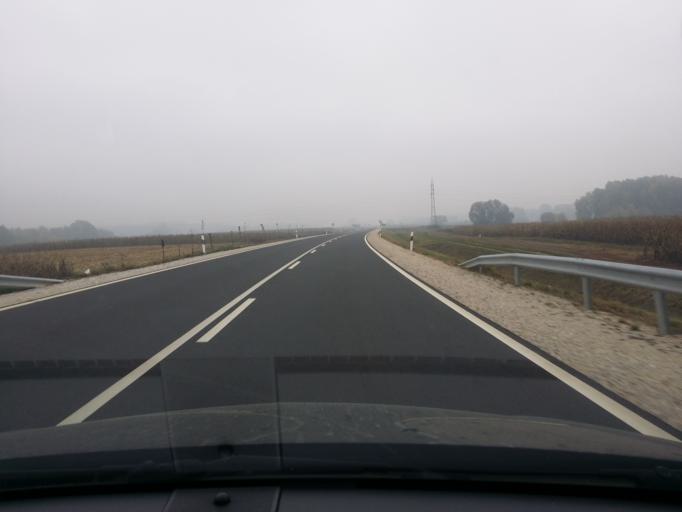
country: HU
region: Szabolcs-Szatmar-Bereg
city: Kalmanhaza
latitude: 47.9262
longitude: 21.6435
